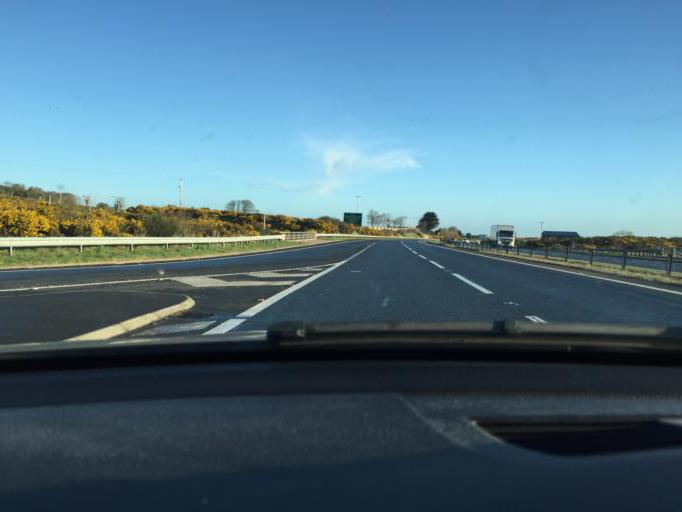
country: GB
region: Northern Ireland
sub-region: Newry and Mourne District
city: Newry
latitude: 54.1673
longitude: -6.3608
